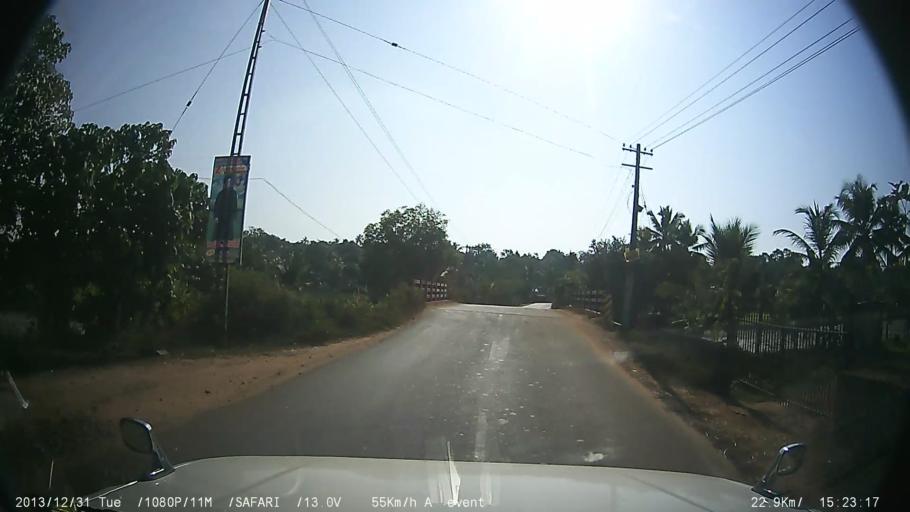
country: IN
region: Kerala
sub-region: Kottayam
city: Vaikam
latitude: 9.6936
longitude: 76.4758
